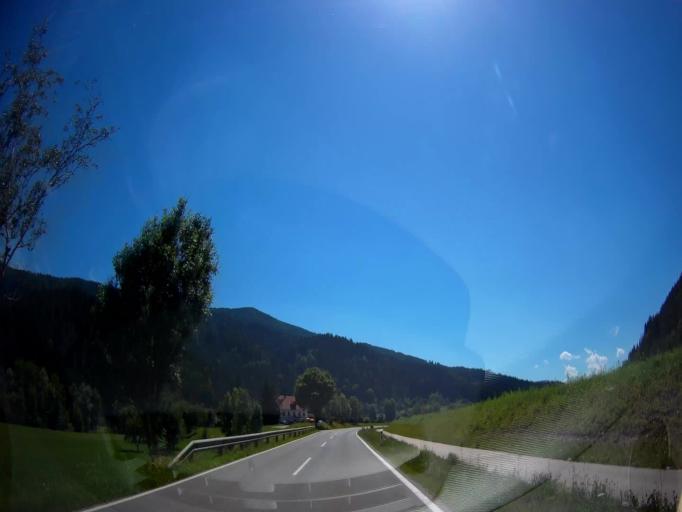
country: AT
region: Carinthia
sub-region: Politischer Bezirk Sankt Veit an der Glan
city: Gurk
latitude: 46.8658
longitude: 14.2537
